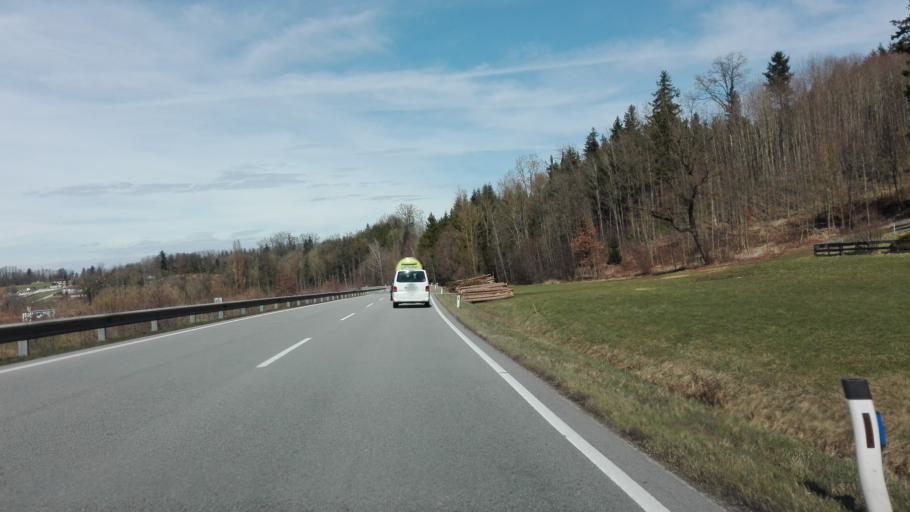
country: AT
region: Upper Austria
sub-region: Politischer Bezirk Ried im Innkreis
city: Ried im Innkreis
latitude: 48.3065
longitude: 13.6353
